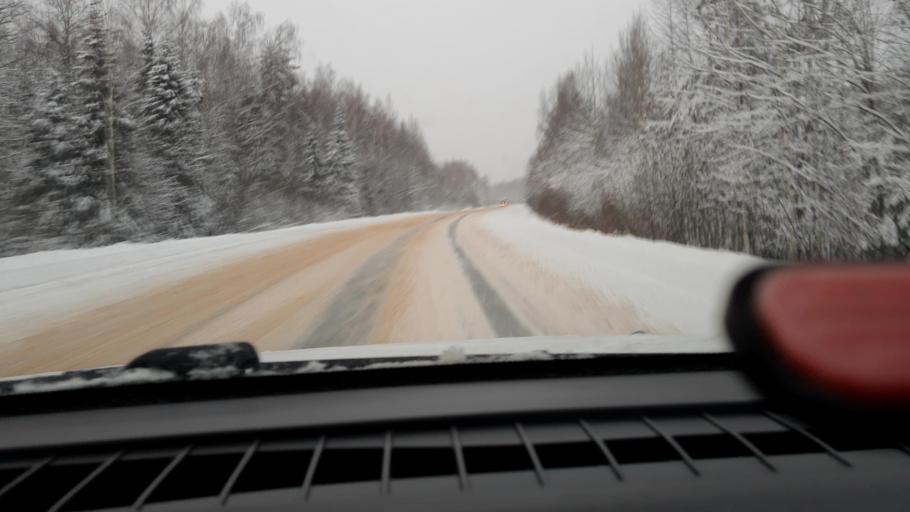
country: RU
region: Nizjnij Novgorod
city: Prudy
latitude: 57.3634
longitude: 46.1829
